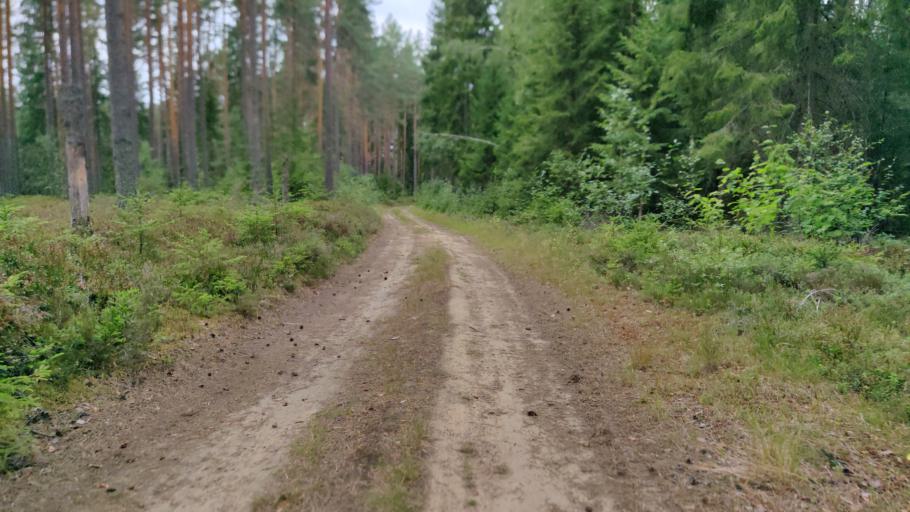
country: SE
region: Vaermland
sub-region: Hagfors Kommun
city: Hagfors
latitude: 60.0135
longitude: 13.5636
